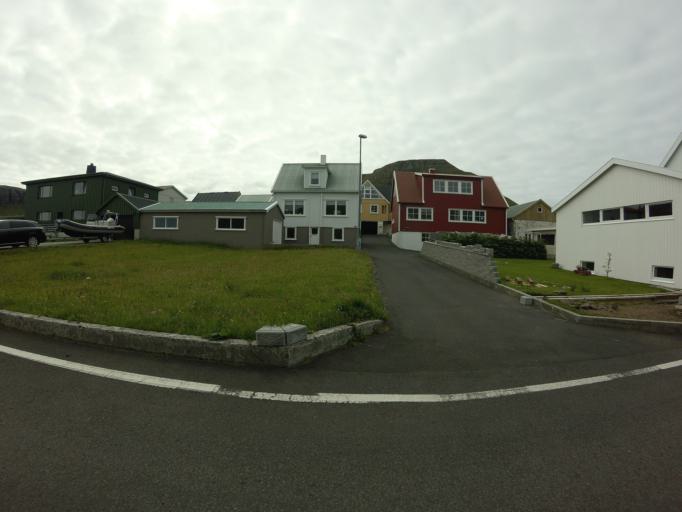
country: FO
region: Suduroy
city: Tvoroyri
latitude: 61.5979
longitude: -6.9495
